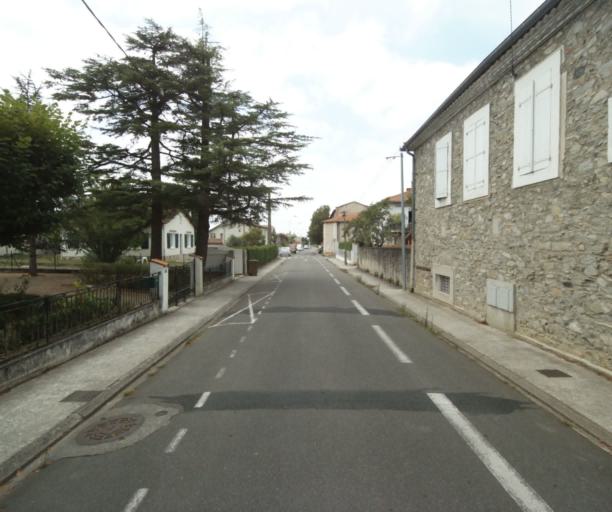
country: FR
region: Midi-Pyrenees
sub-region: Departement de la Haute-Garonne
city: Revel
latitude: 43.4552
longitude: 2.0128
